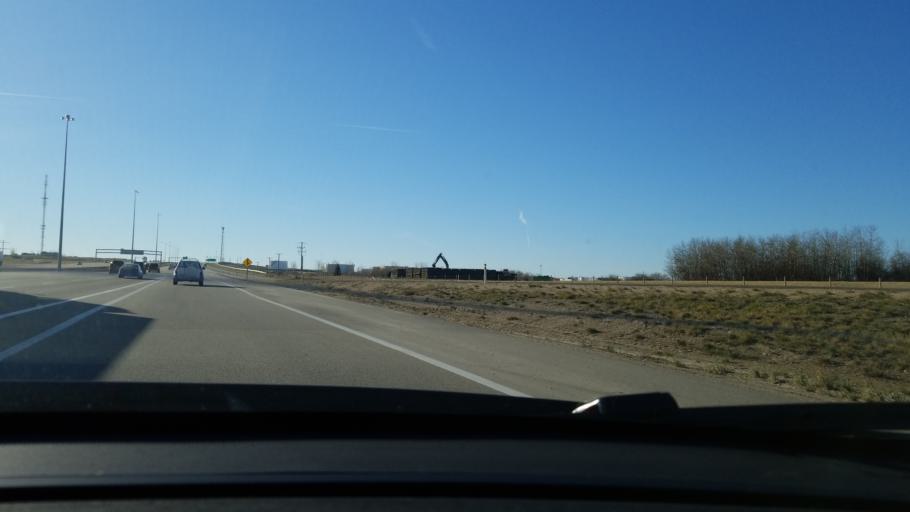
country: CA
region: Alberta
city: Sherwood Park
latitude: 53.5375
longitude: -113.3435
